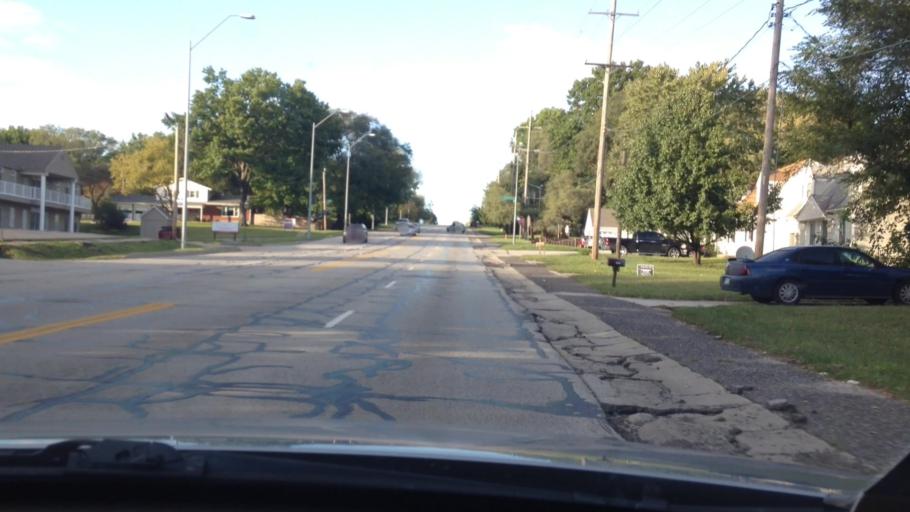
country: US
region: Missouri
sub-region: Platte County
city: Riverside
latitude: 39.1728
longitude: -94.5767
